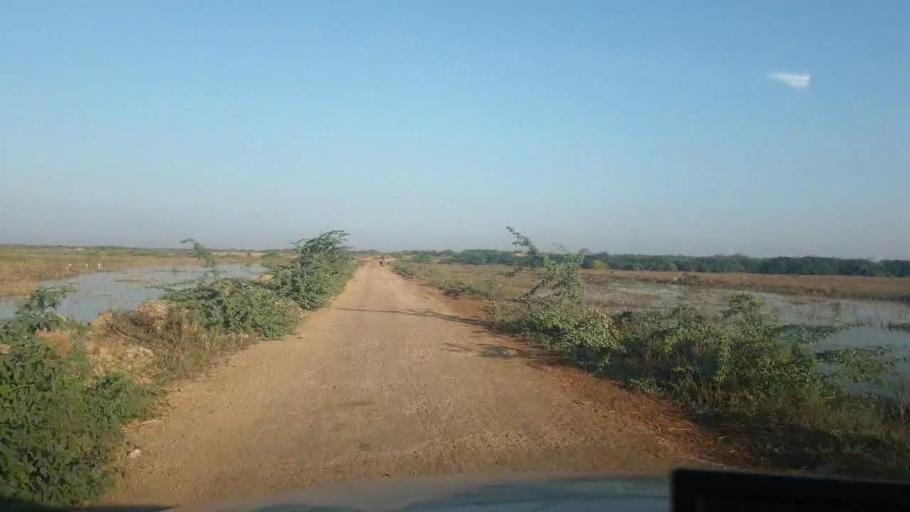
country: PK
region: Sindh
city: Thatta
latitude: 24.7040
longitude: 67.8495
